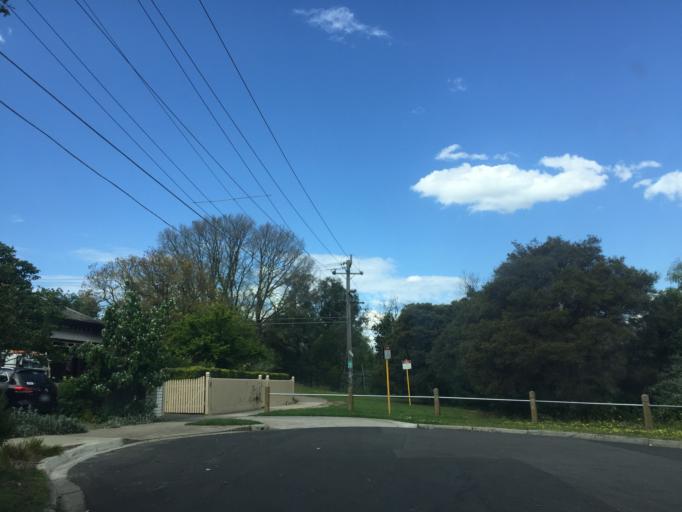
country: AU
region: Victoria
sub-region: Darebin
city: Northcote
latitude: -37.7826
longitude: 145.0012
